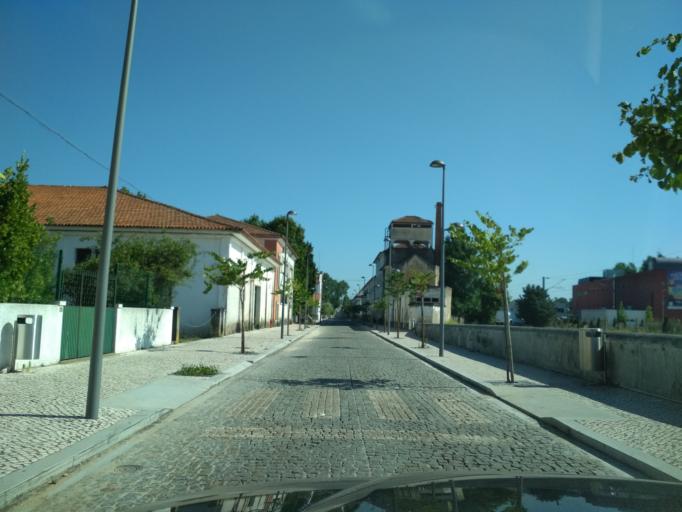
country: PT
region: Aveiro
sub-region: Mealhada
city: Mealhada
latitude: 40.3746
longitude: -8.4534
